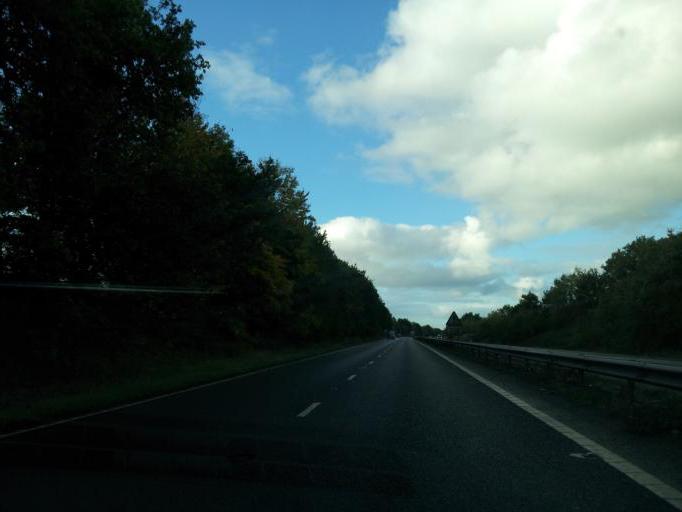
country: GB
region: England
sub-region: Norfolk
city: Brundall
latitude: 52.6374
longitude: 1.4429
